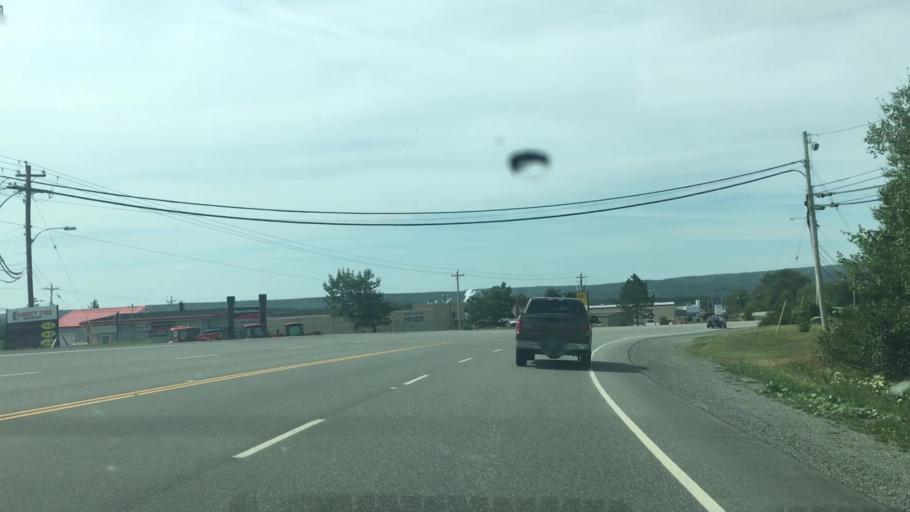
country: CA
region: Nova Scotia
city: Port Hawkesbury
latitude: 45.6164
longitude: -61.3368
